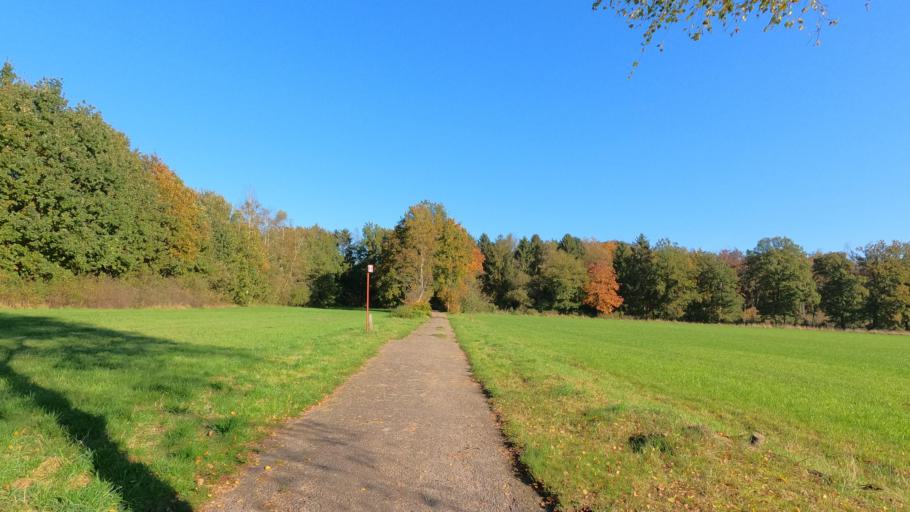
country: BE
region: Flanders
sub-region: Provincie Antwerpen
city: Schilde
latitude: 51.2823
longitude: 4.6305
